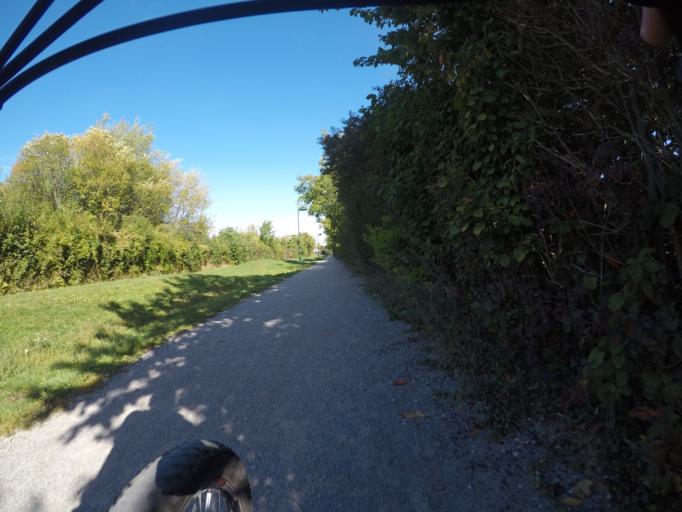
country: AT
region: Lower Austria
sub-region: Politischer Bezirk Modling
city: Brunn am Gebirge
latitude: 48.1061
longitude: 16.2989
